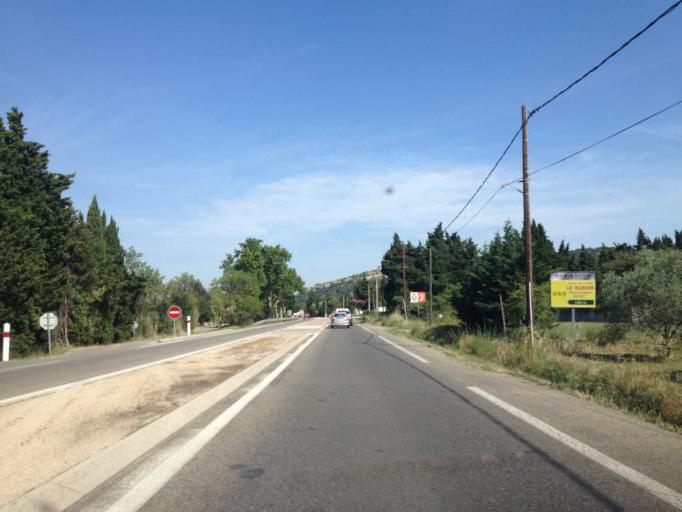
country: FR
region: Provence-Alpes-Cote d'Azur
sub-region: Departement du Vaucluse
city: Mornas
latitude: 44.1939
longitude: 4.7411
